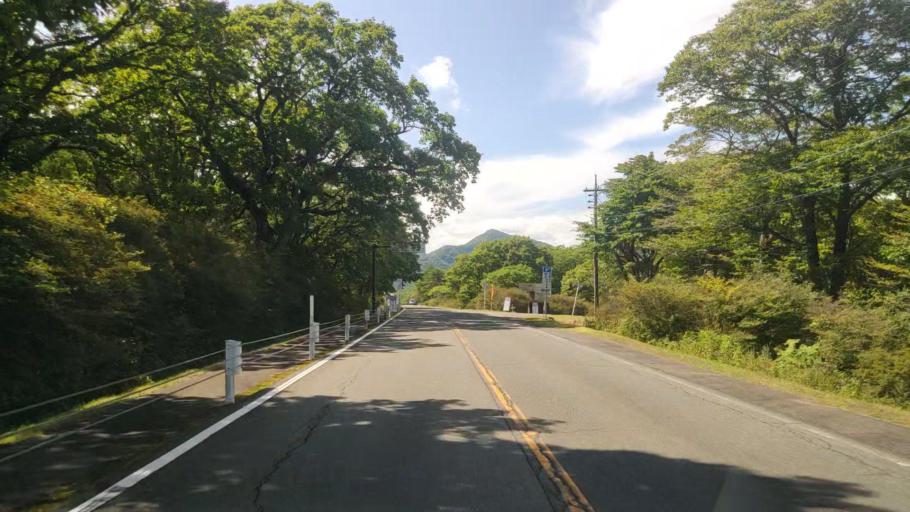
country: JP
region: Gunma
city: Shibukawa
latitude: 36.4801
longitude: 138.8944
